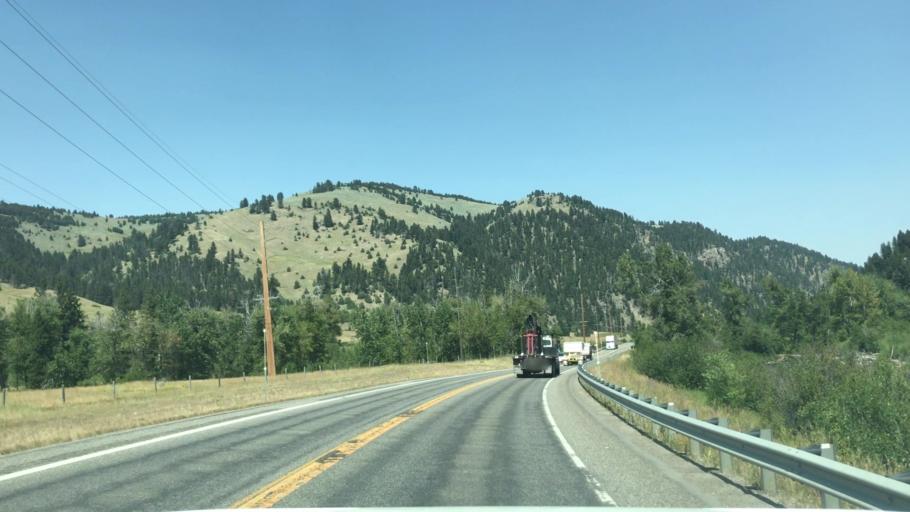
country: US
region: Montana
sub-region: Gallatin County
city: Four Corners
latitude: 45.4917
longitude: -111.2725
